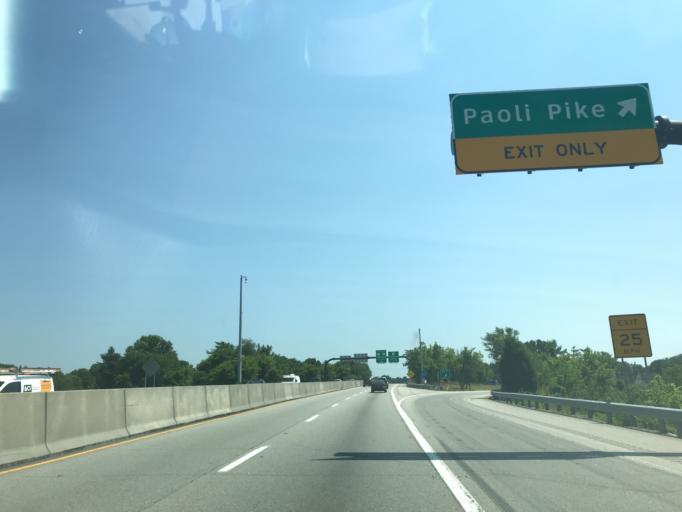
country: US
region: Pennsylvania
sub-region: Chester County
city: West Chester
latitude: 39.9732
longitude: -75.5839
